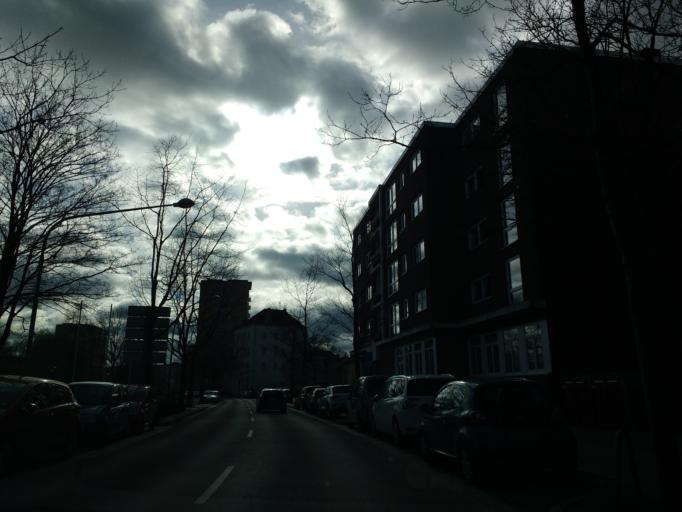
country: DE
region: Bremen
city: Bremerhaven
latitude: 53.5457
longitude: 8.5800
